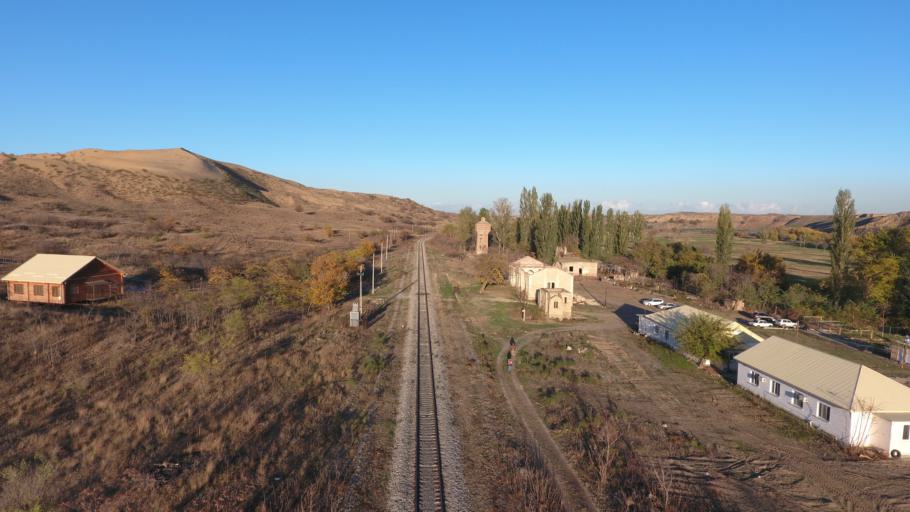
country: RU
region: Dagestan
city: Korkmaskala
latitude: 43.0025
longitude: 47.2367
